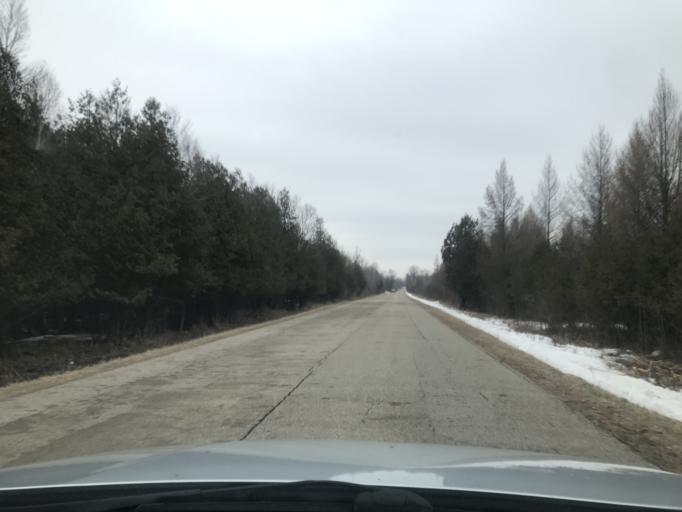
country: US
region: Wisconsin
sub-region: Marinette County
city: Peshtigo
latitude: 45.1334
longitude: -88.0075
